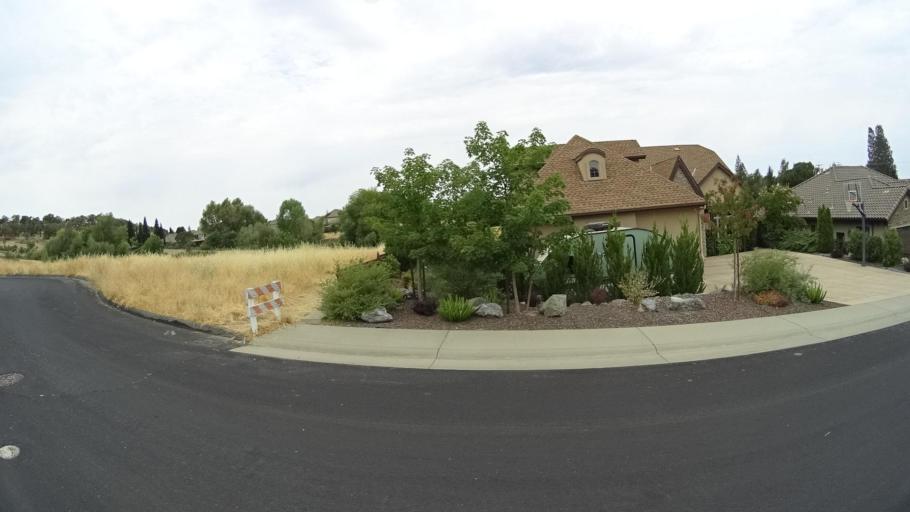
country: US
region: California
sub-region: Placer County
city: Rocklin
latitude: 38.7804
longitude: -121.2179
